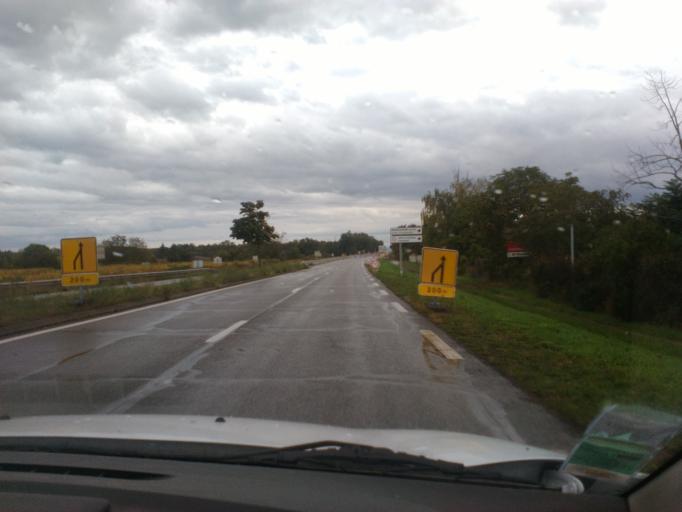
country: FR
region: Alsace
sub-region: Departement du Haut-Rhin
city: Ingersheim
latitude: 48.1020
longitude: 7.3060
